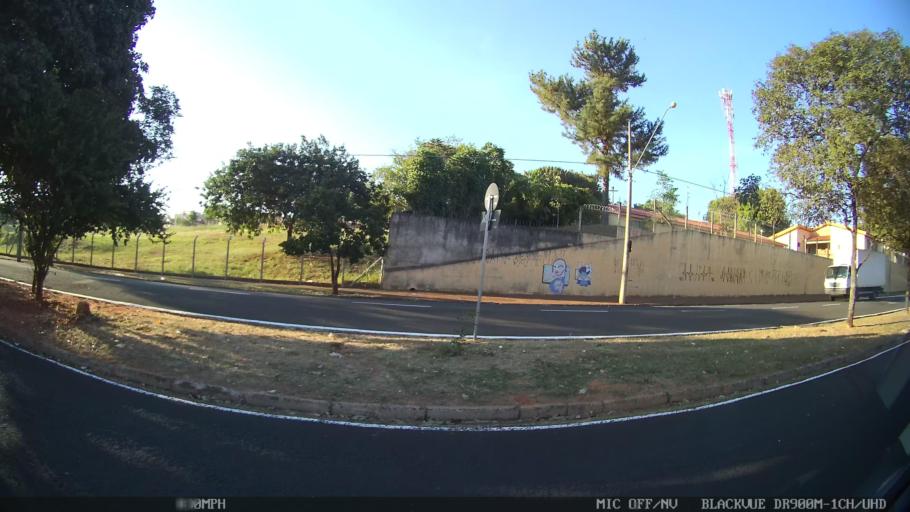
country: BR
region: Sao Paulo
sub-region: Sao Jose Do Rio Preto
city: Sao Jose do Rio Preto
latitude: -20.7876
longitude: -49.3634
